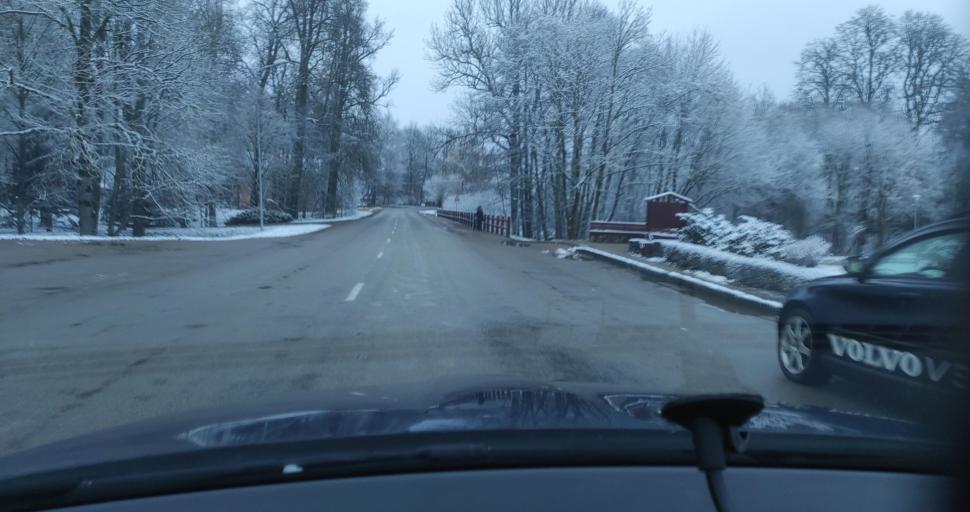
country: LV
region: Skrunda
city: Skrunda
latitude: 56.8720
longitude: 22.2364
